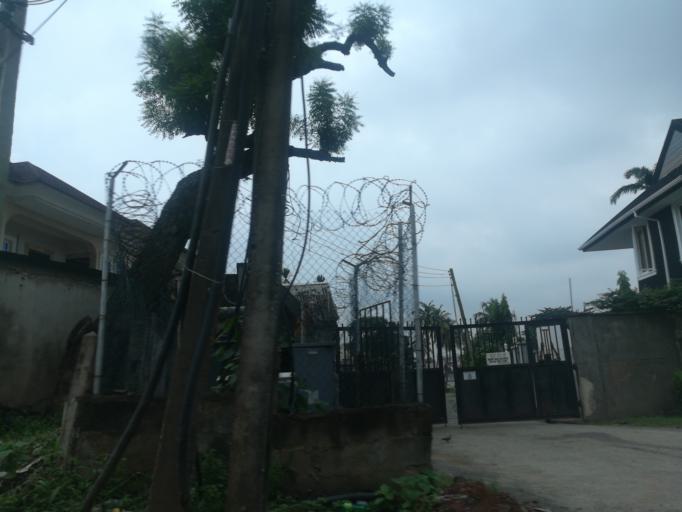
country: NG
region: Lagos
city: Ojota
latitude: 6.5687
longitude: 3.3711
